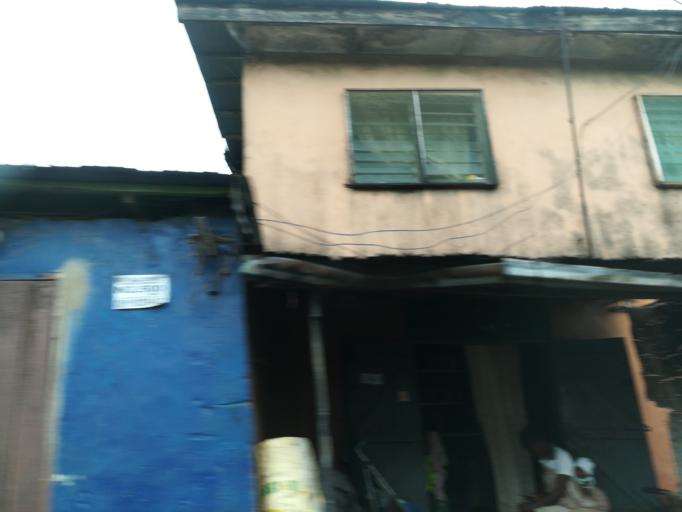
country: NG
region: Lagos
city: Oshodi
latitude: 6.5592
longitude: 3.3403
